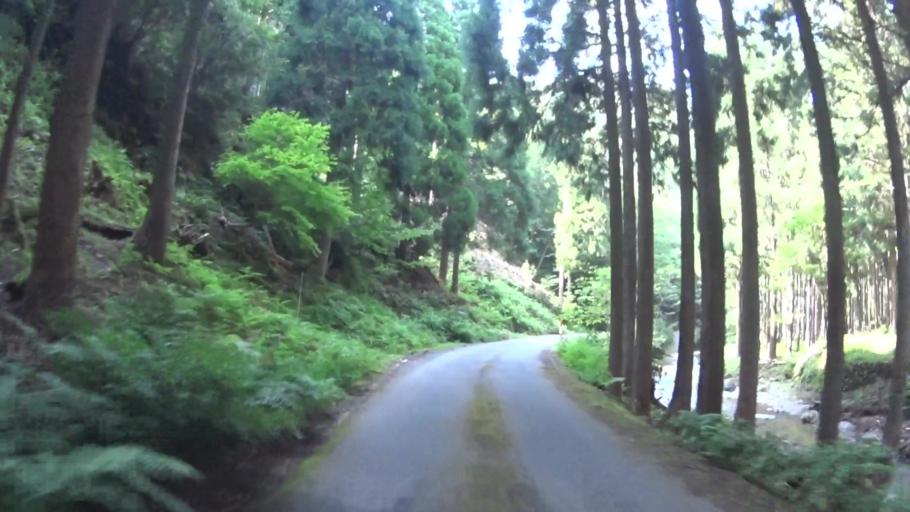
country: JP
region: Fukui
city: Obama
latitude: 35.2797
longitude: 135.6408
